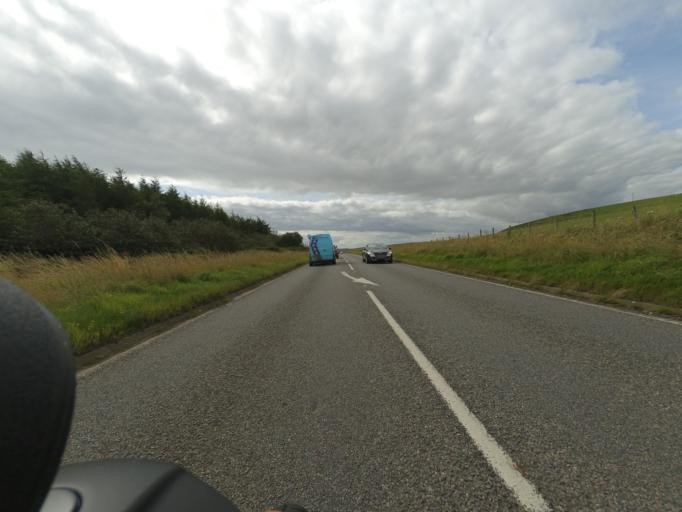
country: GB
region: Scotland
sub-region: Aberdeenshire
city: Inverbervie
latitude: 56.8769
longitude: -2.2586
